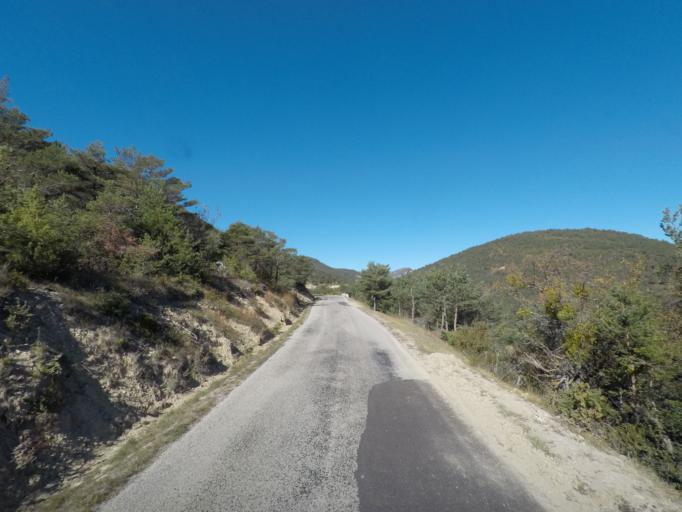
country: FR
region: Rhone-Alpes
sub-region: Departement de la Drome
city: Die
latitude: 44.5627
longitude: 5.3174
